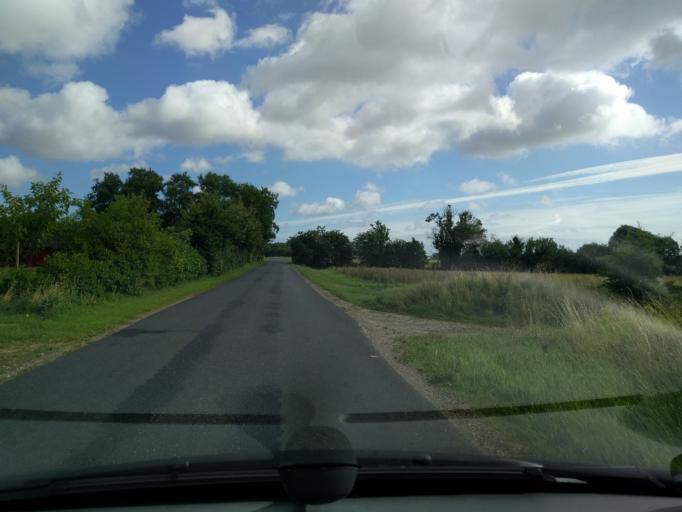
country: DK
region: South Denmark
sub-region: Kerteminde Kommune
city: Langeskov
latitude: 55.3866
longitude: 10.5893
